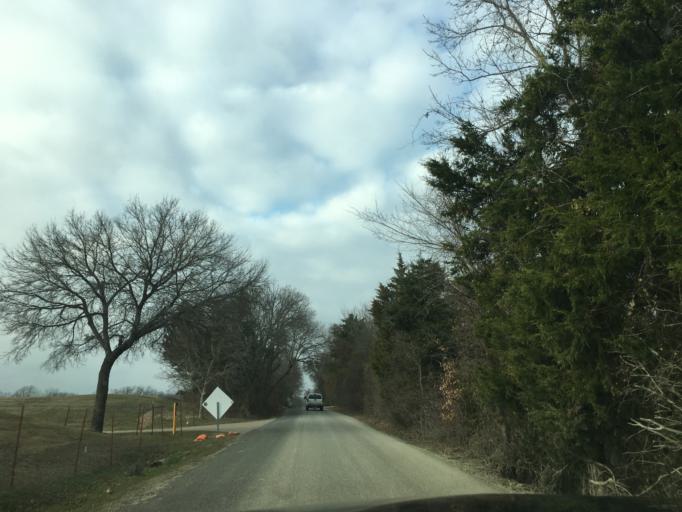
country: US
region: Texas
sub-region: Ellis County
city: Red Oak
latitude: 32.4864
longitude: -96.7967
